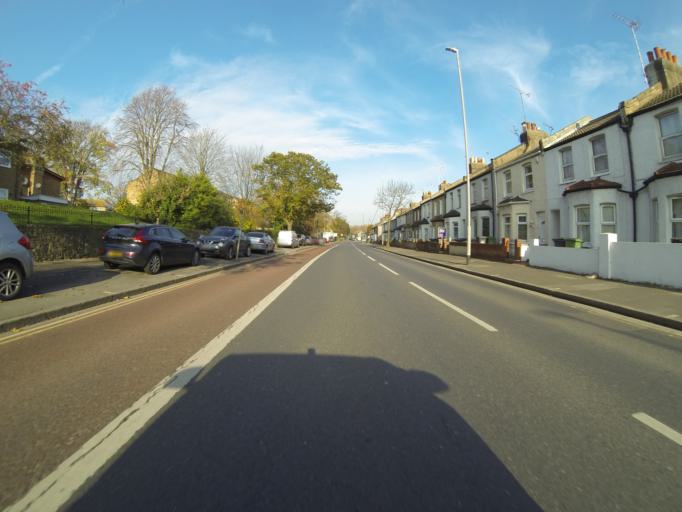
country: GB
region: England
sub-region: Kent
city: Dartford
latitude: 51.4358
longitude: 0.2158
